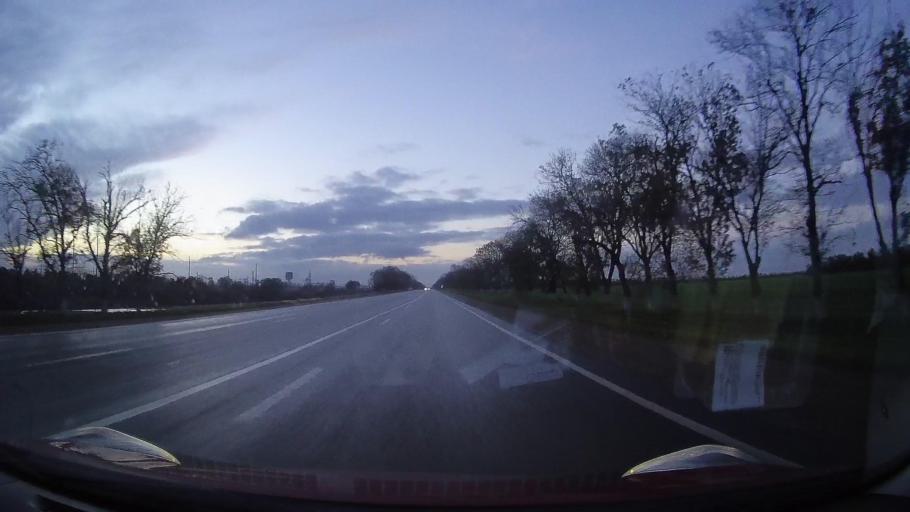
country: RU
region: Krasnodarskiy
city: Zavetnyy
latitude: 44.8846
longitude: 41.2201
